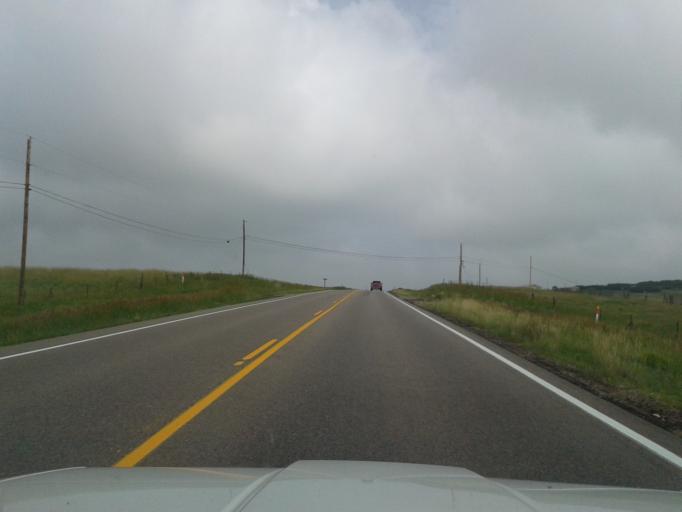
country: US
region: Colorado
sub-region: Elbert County
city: Ponderosa Park
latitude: 39.2675
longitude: -104.7281
